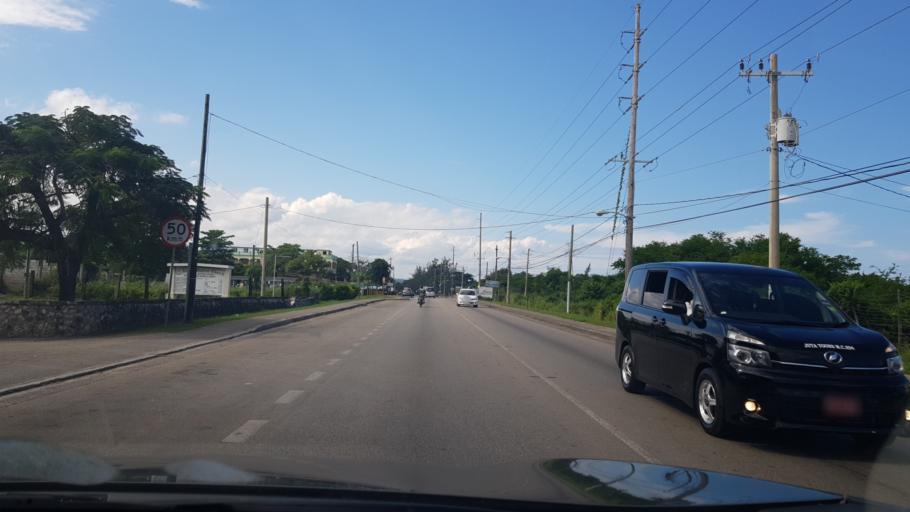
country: JM
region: Saint Ann
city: Runaway Bay
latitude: 18.4659
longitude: -77.3148
